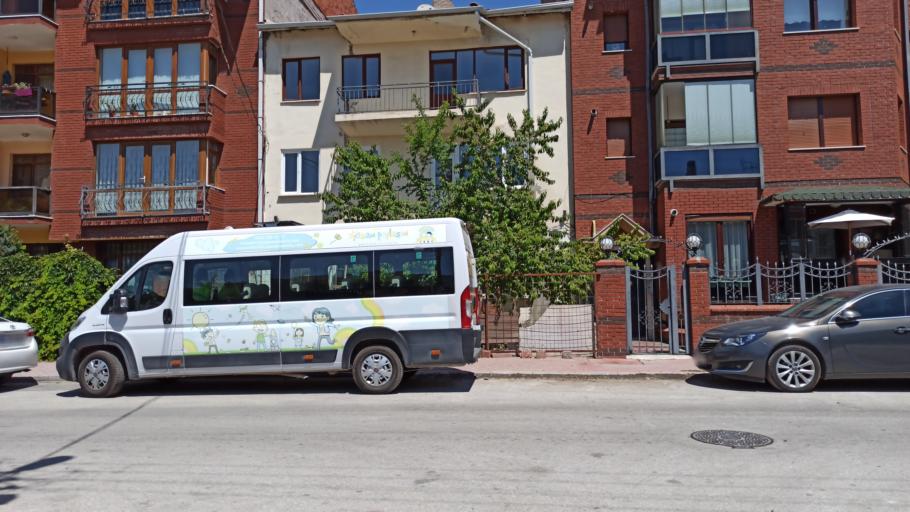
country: TR
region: Eskisehir
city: Eskisehir
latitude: 39.7668
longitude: 30.5039
